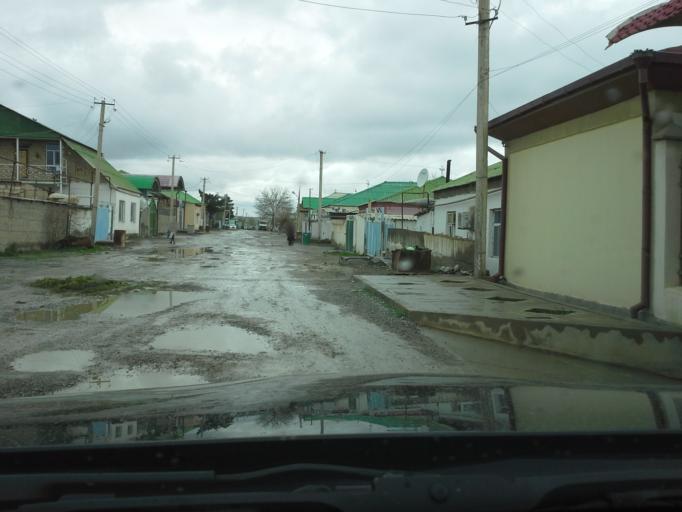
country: TM
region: Ahal
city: Abadan
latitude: 37.9646
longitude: 58.2132
